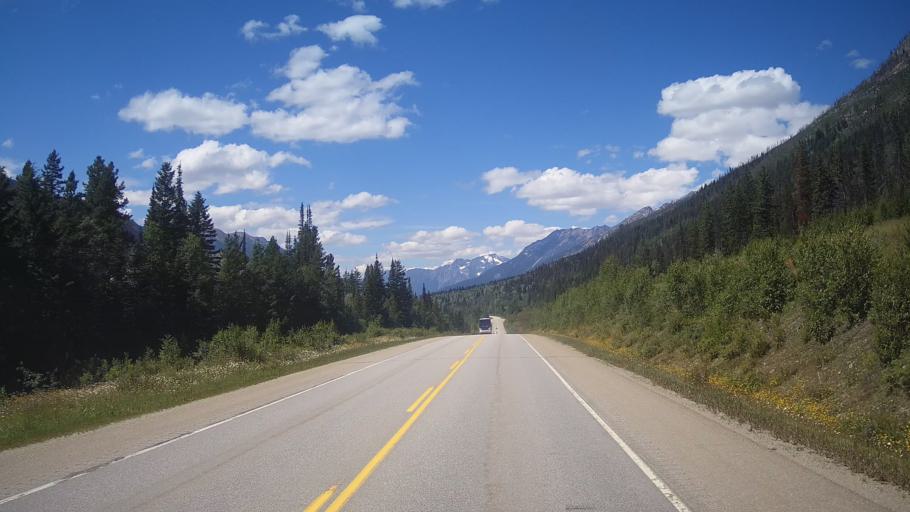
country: CA
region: Alberta
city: Jasper Park Lodge
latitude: 52.9659
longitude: -118.9218
